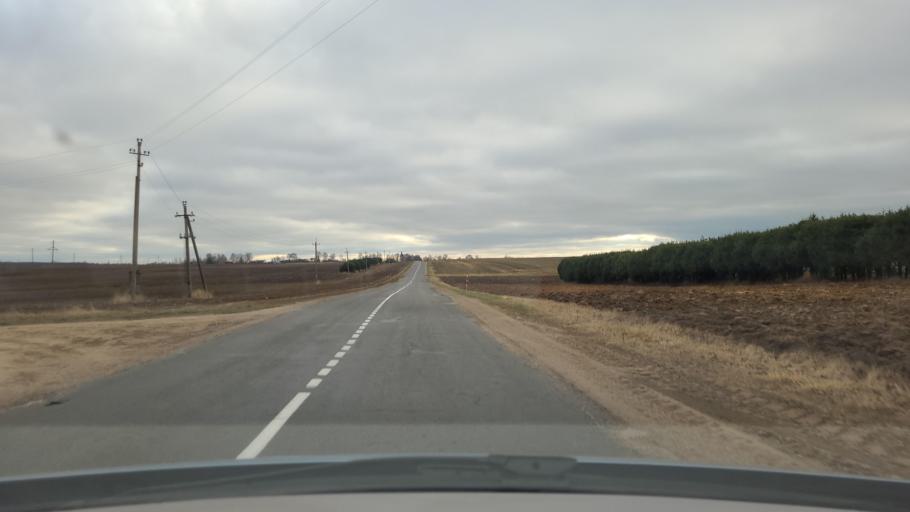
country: BY
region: Minsk
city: Khalopyenichy
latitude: 54.4502
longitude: 28.9874
